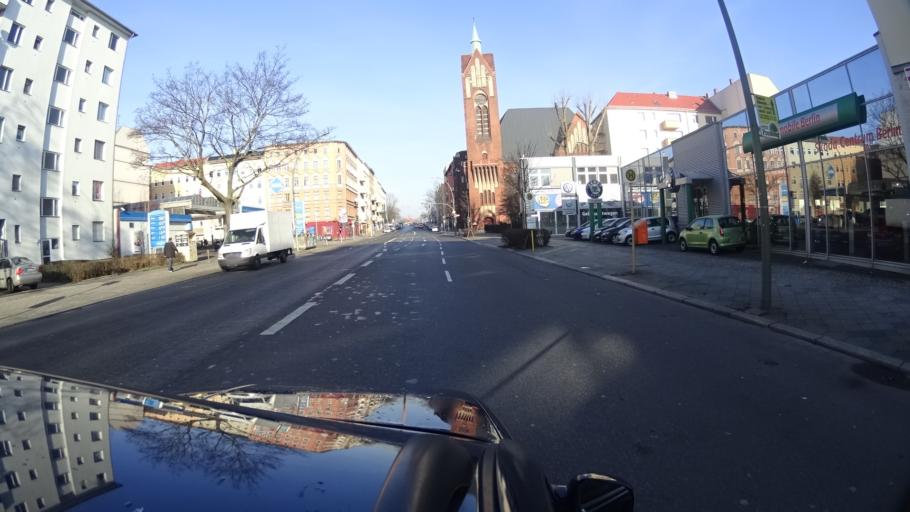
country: DE
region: Berlin
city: Moabit
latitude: 52.5303
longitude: 13.3286
